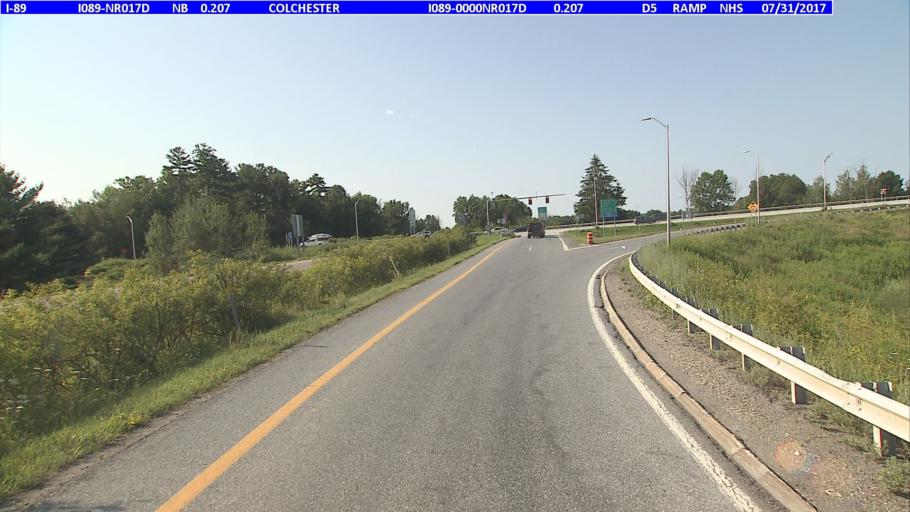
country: US
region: Vermont
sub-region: Chittenden County
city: Colchester
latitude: 44.5909
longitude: -73.1681
